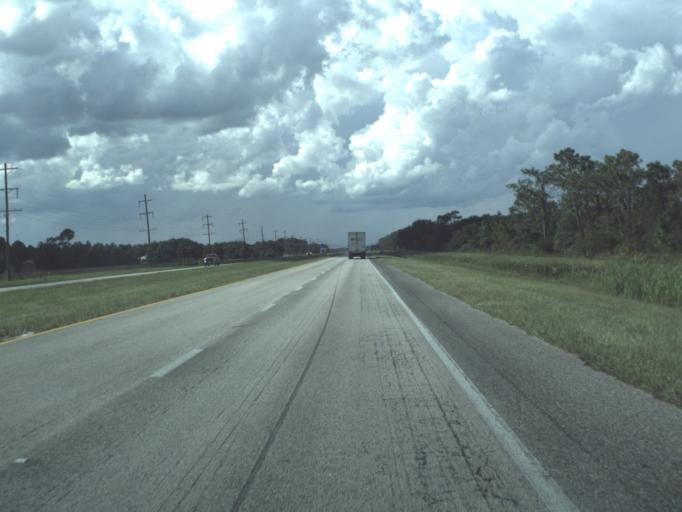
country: US
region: Florida
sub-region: Polk County
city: Babson Park
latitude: 27.8172
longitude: -81.3291
